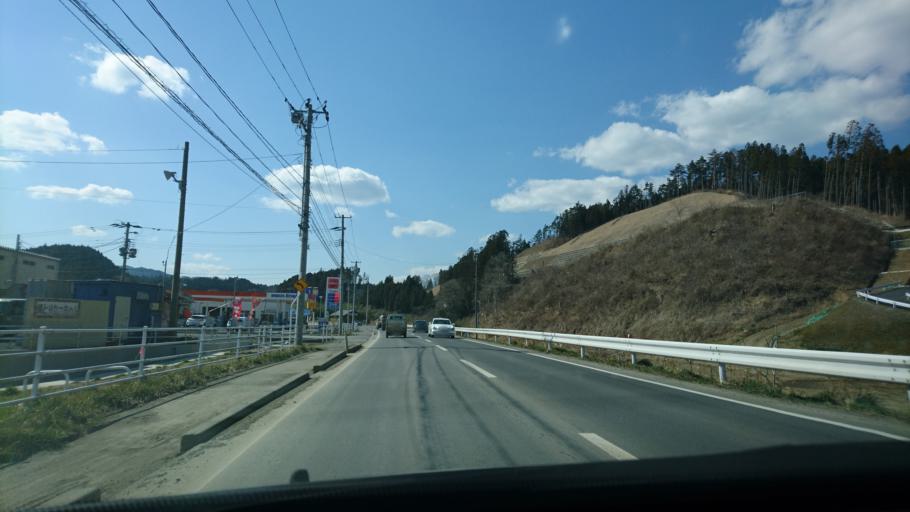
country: JP
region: Miyagi
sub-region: Oshika Gun
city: Onagawa Cho
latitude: 38.6878
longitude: 141.4393
